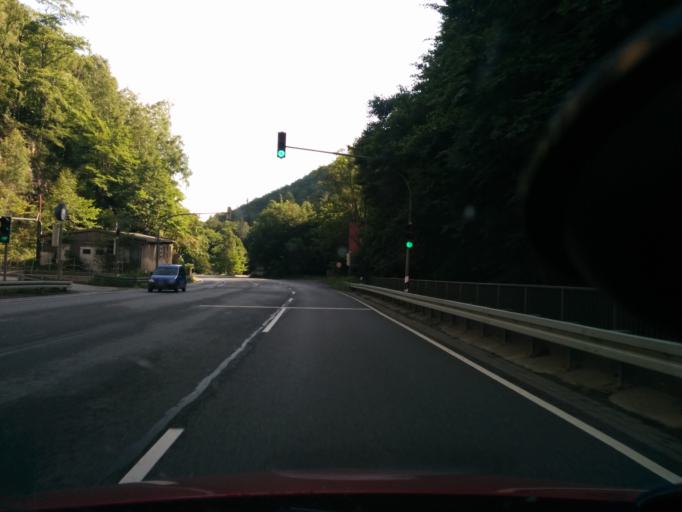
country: DE
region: Lower Saxony
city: Bad Harzburg
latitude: 51.8574
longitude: 10.5532
